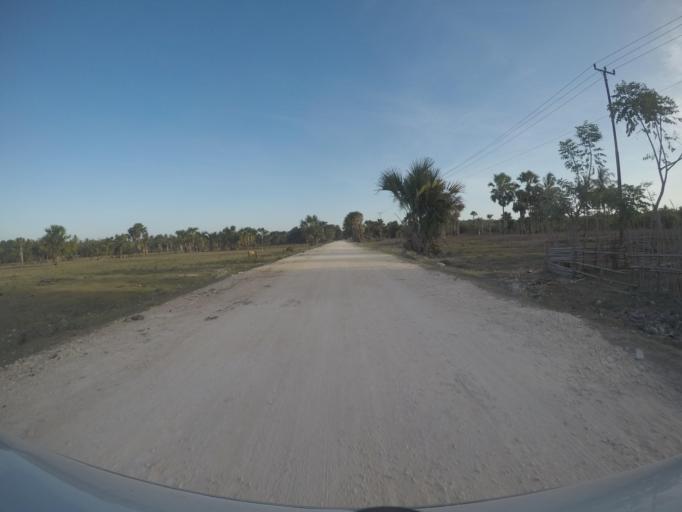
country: TL
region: Viqueque
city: Viqueque
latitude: -8.8889
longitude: 126.5069
